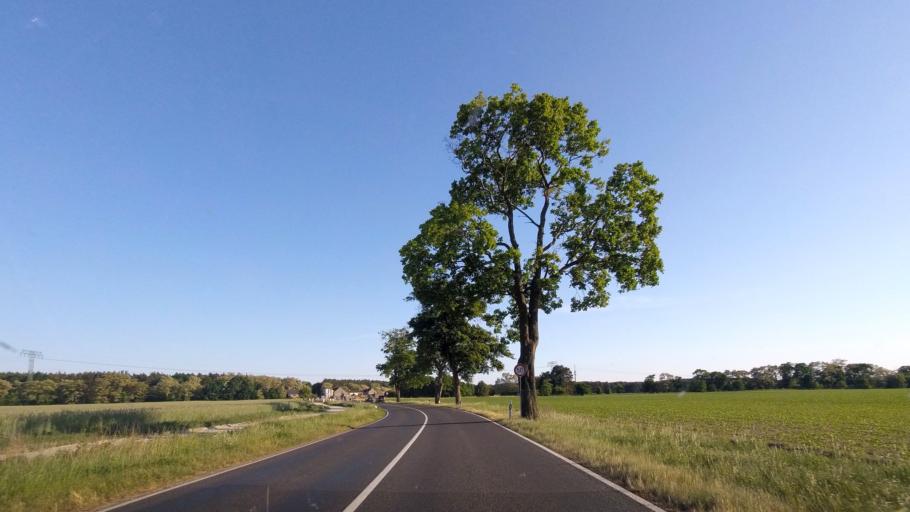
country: DE
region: Brandenburg
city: Golzow
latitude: 52.3374
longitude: 12.6026
